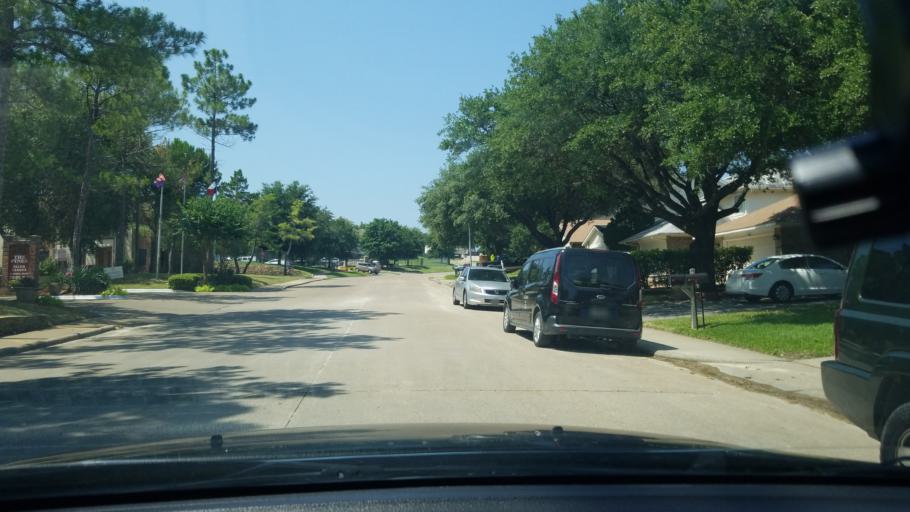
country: US
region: Texas
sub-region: Dallas County
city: Sunnyvale
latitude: 32.8307
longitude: -96.6013
